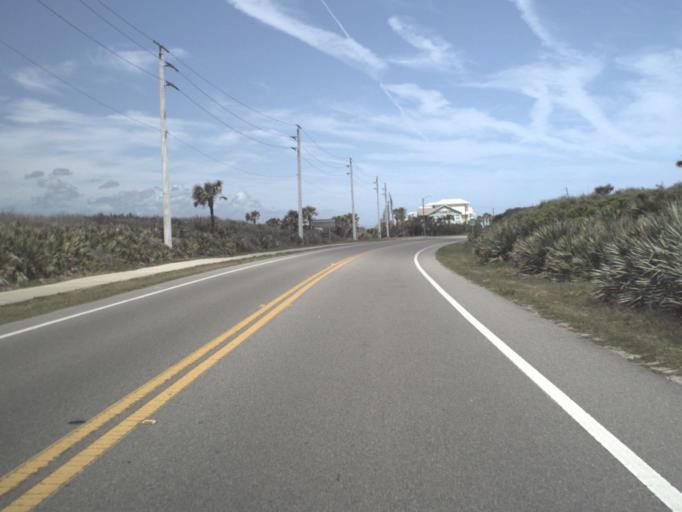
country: US
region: Florida
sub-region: Flagler County
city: Flagler Beach
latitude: 29.4399
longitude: -81.1091
